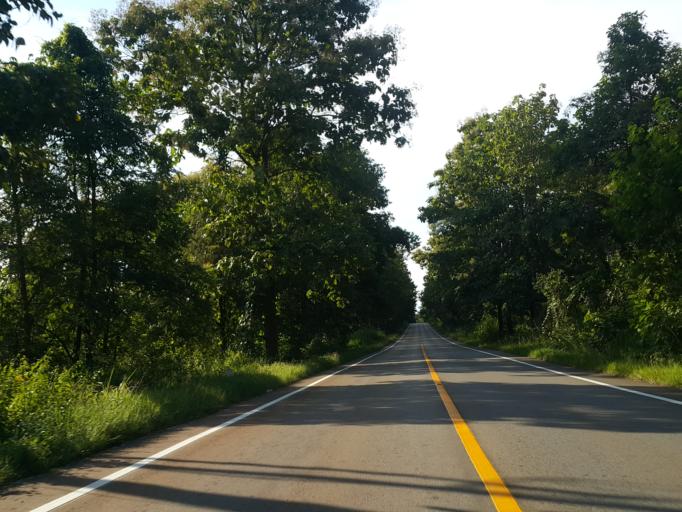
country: TH
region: Chiang Mai
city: Mae Taeng
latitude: 19.0780
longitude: 99.1058
